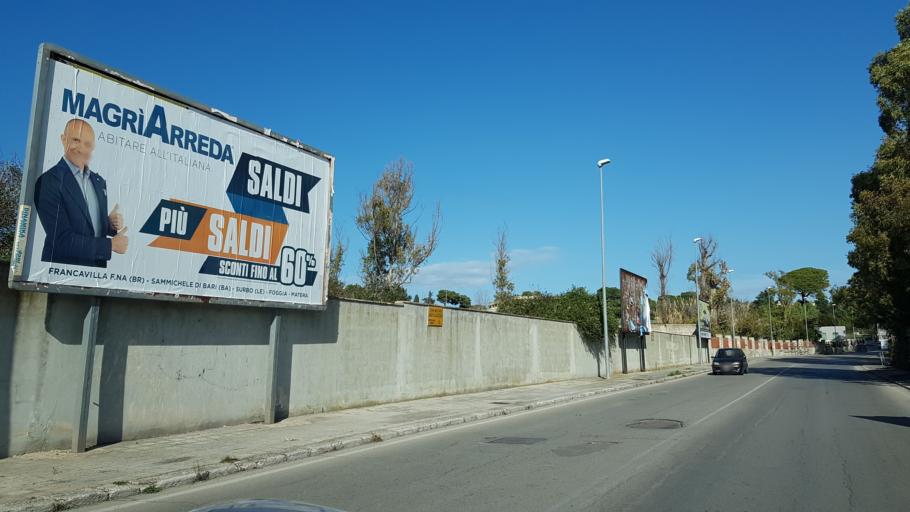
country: IT
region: Apulia
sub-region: Provincia di Brindisi
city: Brindisi
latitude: 40.6413
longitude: 17.9283
